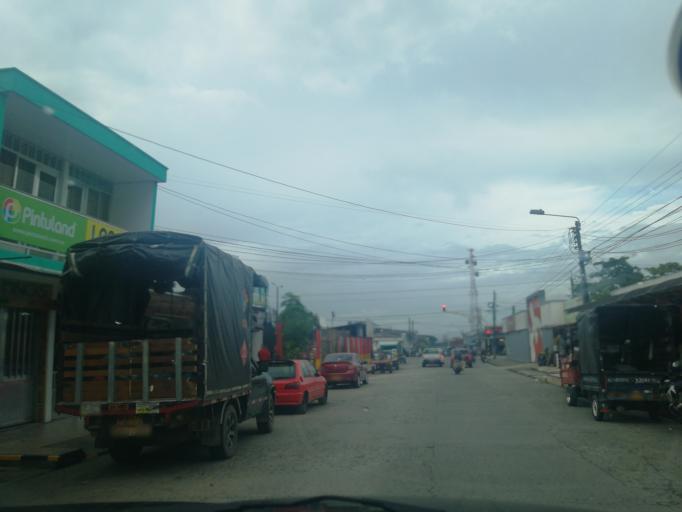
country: CO
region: Meta
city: Acacias
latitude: 3.9864
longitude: -73.7671
